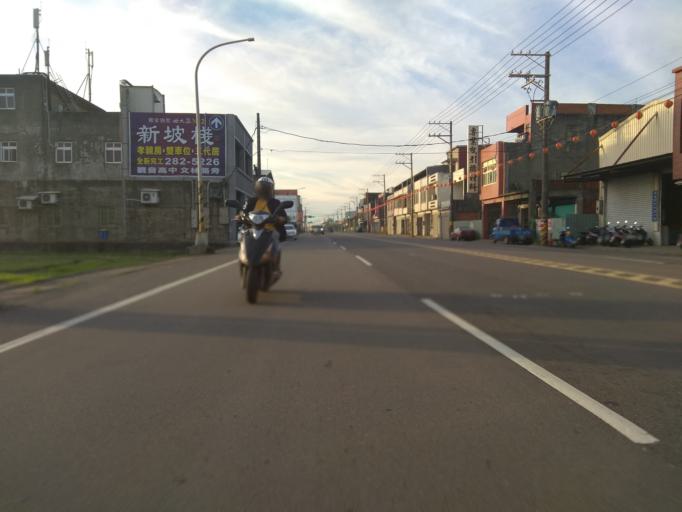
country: TW
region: Taiwan
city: Taoyuan City
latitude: 25.0034
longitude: 121.1518
